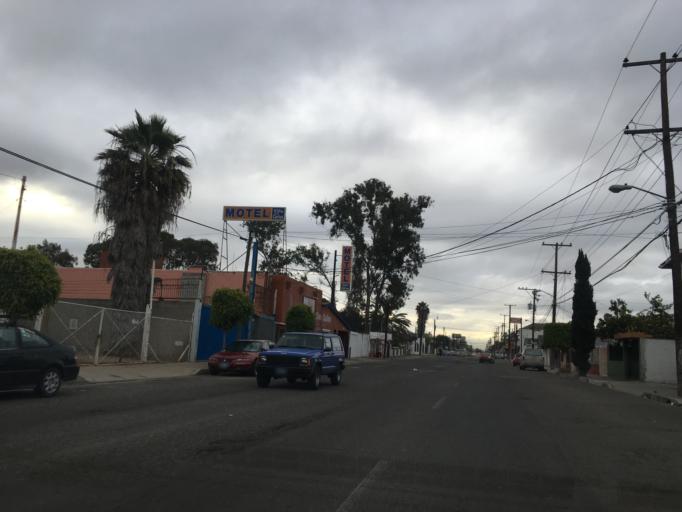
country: MX
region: Baja California
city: Tijuana
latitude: 32.5387
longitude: -117.0596
